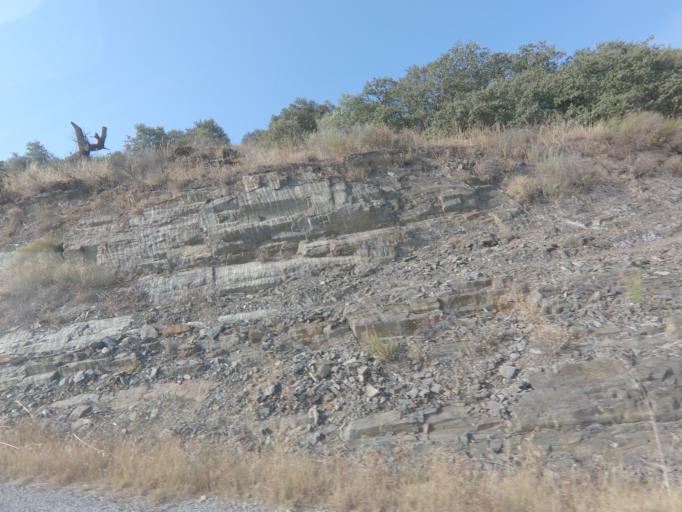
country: PT
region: Viseu
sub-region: Tabuaco
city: Tabuaco
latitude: 41.1296
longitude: -7.5425
